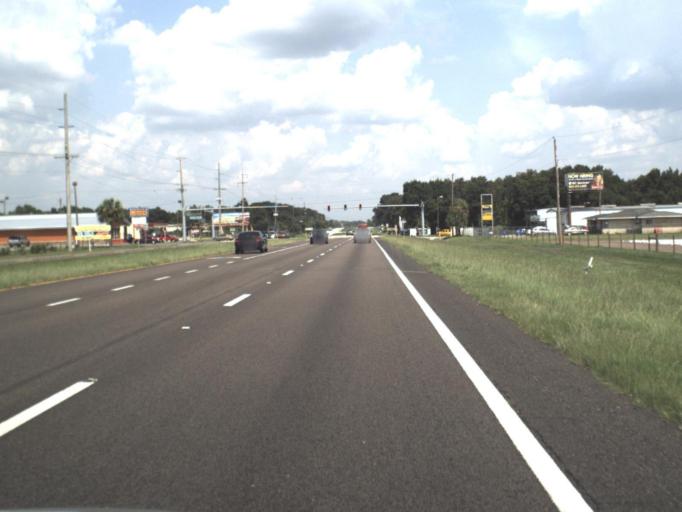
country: US
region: Florida
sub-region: Polk County
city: Willow Oak
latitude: 27.9271
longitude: -82.0574
